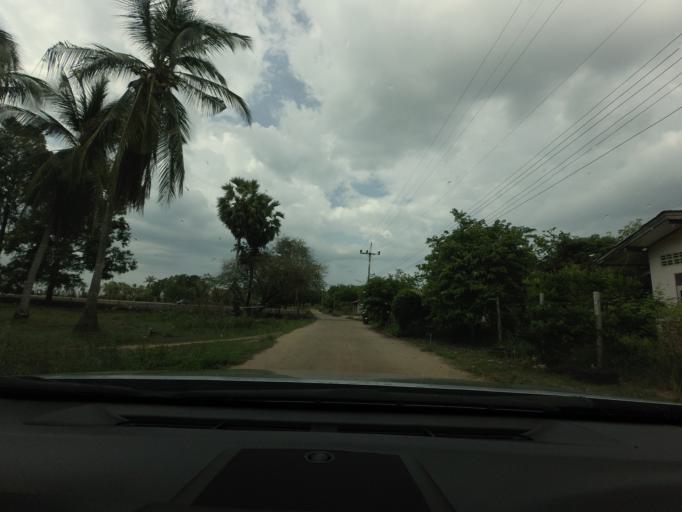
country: TH
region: Songkhla
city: Chana
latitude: 6.9526
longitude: 100.8350
